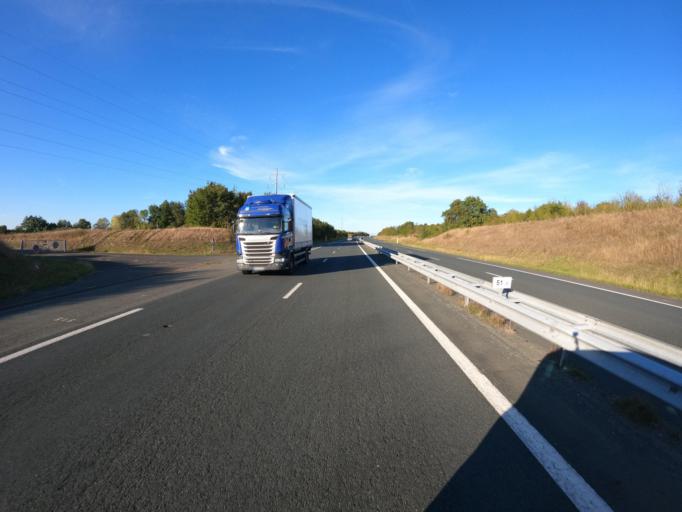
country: FR
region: Pays de la Loire
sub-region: Departement de Maine-et-Loire
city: Mazieres-en-Mauges
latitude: 47.0507
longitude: -0.8363
